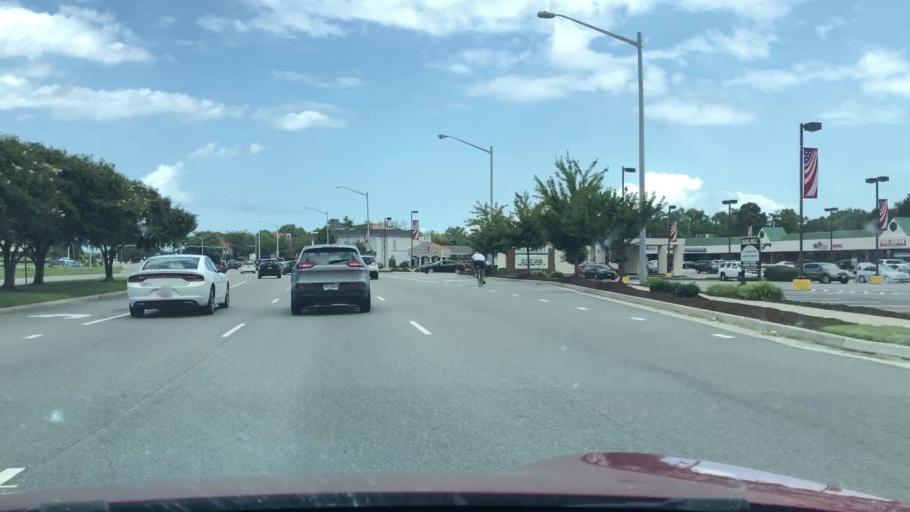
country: US
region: Virginia
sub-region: City of Chesapeake
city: Chesapeake
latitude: 36.8632
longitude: -76.1320
